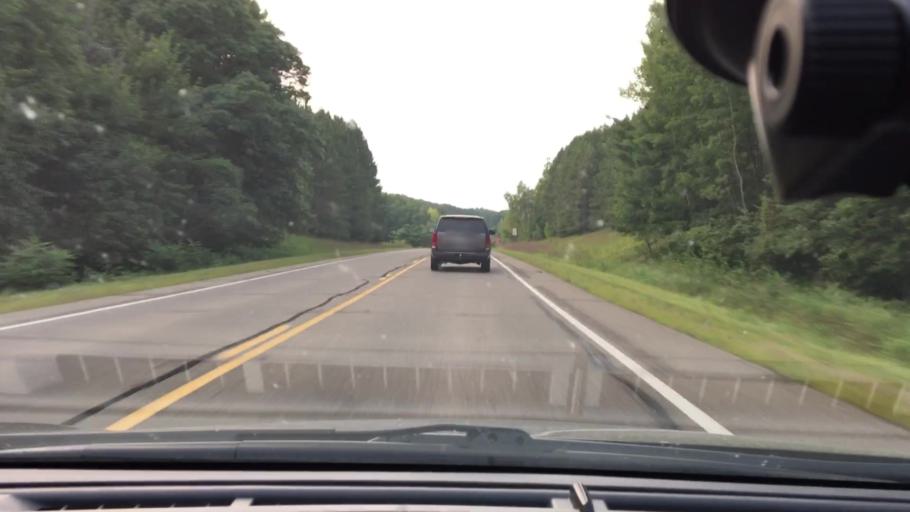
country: US
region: Minnesota
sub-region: Crow Wing County
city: Crosby
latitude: 46.3941
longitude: -93.8764
